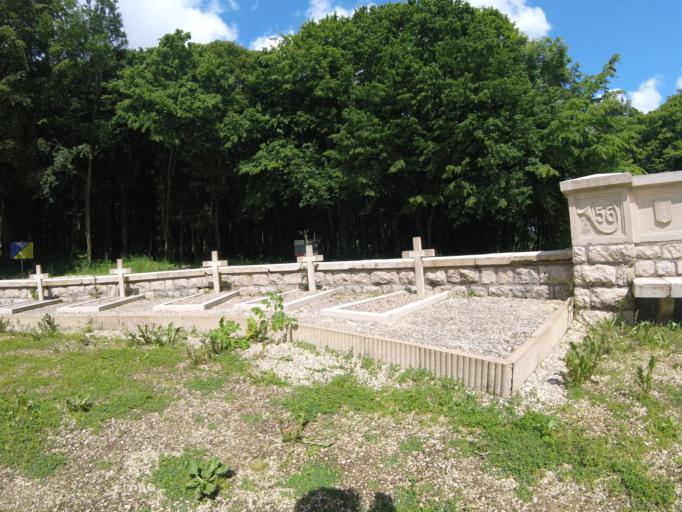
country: FR
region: Lorraine
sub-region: Departement de la Meuse
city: Belleville-sur-Meuse
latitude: 49.2715
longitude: 5.4055
